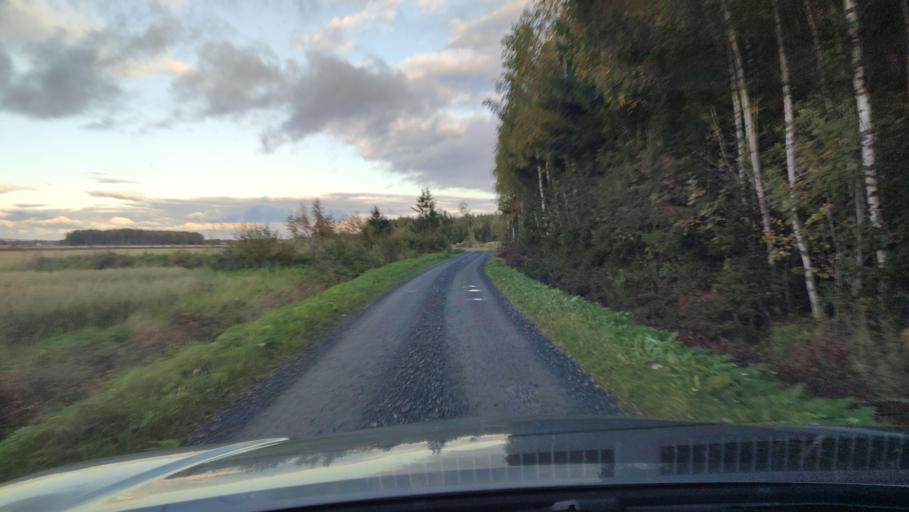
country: FI
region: Ostrobothnia
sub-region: Sydosterbotten
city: Kristinestad
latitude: 62.2516
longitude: 21.4568
